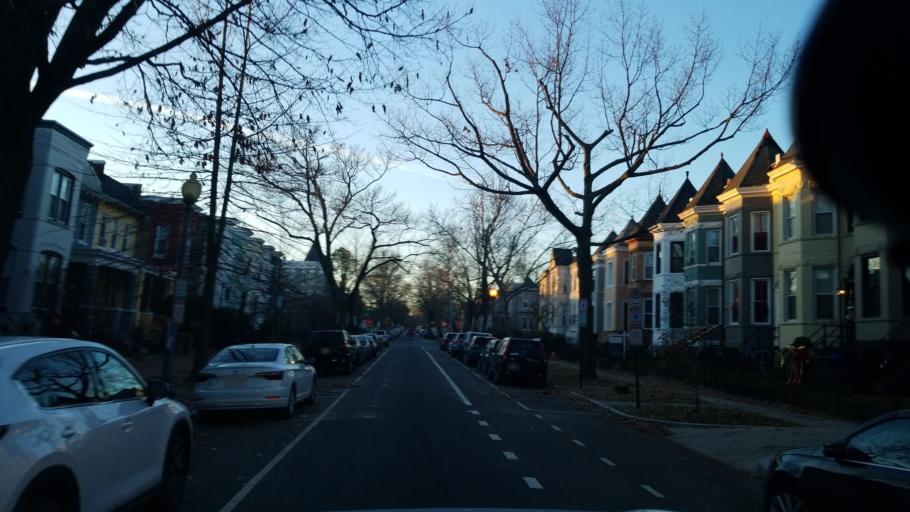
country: US
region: Maryland
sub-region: Prince George's County
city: Mount Rainier
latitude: 38.8982
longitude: -76.9855
